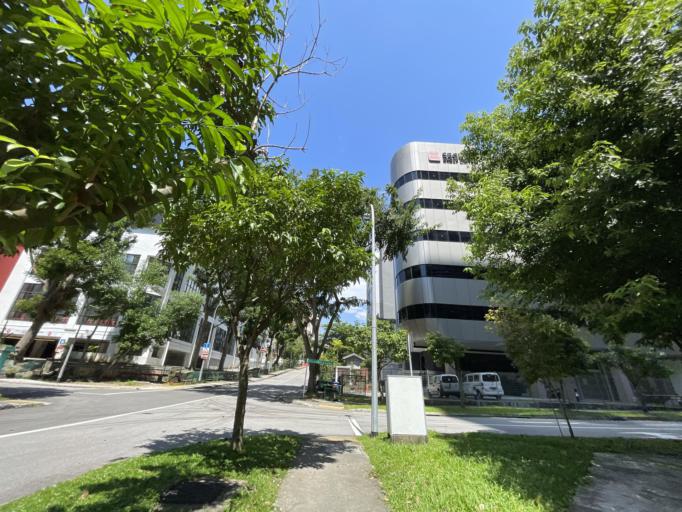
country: SG
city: Singapore
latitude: 1.2754
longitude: 103.7974
